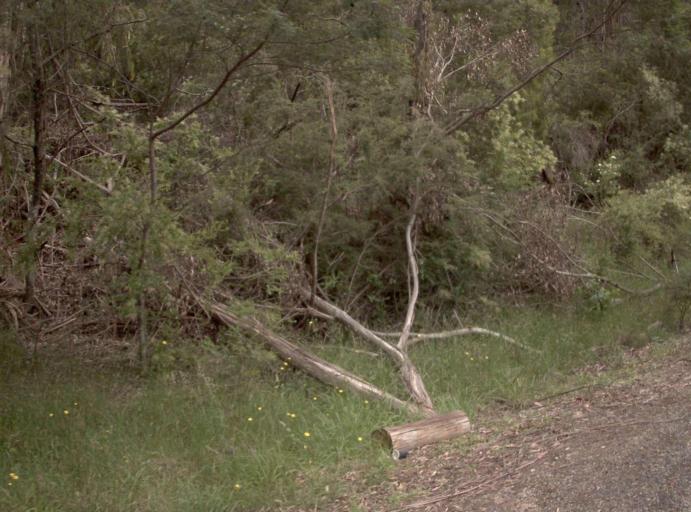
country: AU
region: New South Wales
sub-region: Bombala
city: Bombala
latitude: -37.4269
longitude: 149.1995
